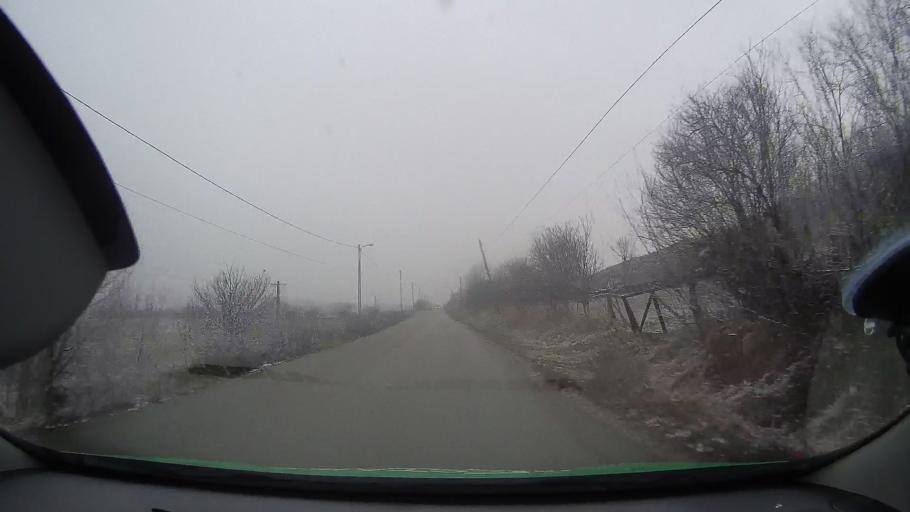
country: RO
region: Alba
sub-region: Comuna Farau
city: Farau
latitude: 46.3386
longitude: 23.9528
